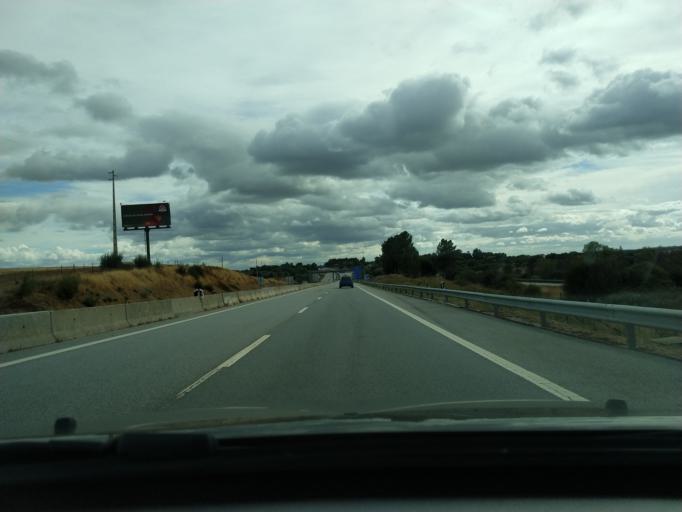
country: PT
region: Castelo Branco
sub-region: Concelho do Fundao
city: Fundao
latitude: 40.0362
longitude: -7.4691
